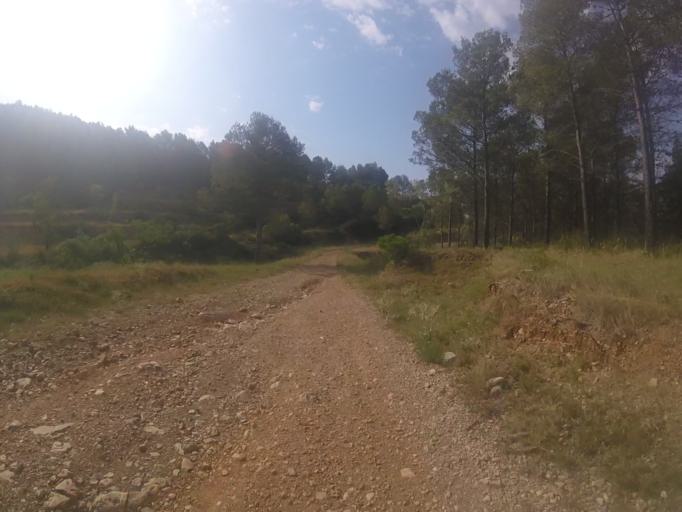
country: ES
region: Valencia
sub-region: Provincia de Castello
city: Cervera del Maestre
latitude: 40.3984
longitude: 0.2056
